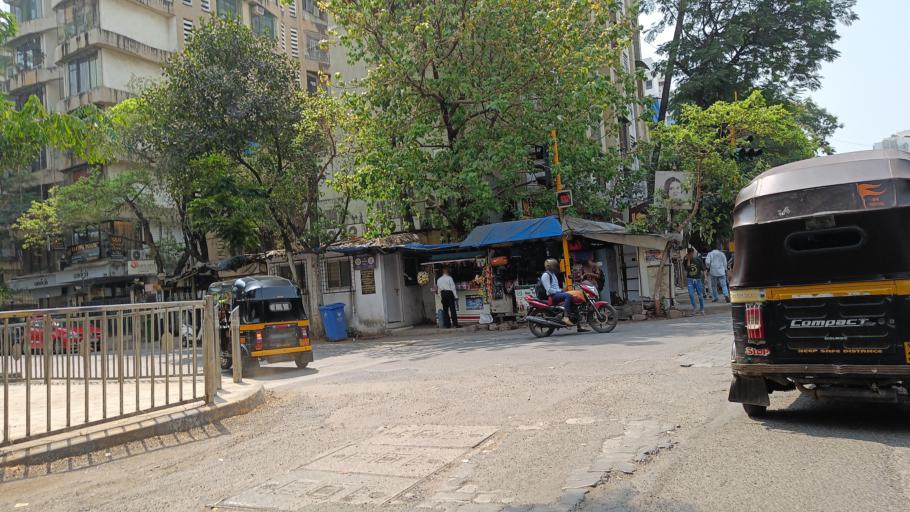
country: IN
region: Maharashtra
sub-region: Mumbai Suburban
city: Powai
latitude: 19.1329
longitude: 72.8258
